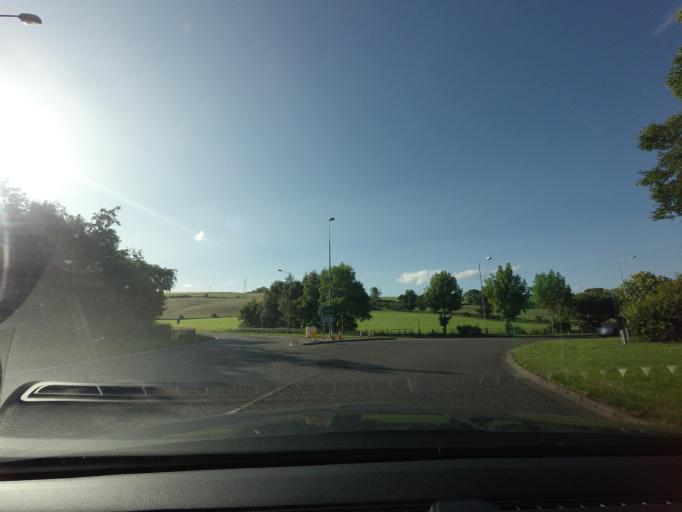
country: GB
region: Scotland
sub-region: Highland
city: Conon Bridge
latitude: 57.5791
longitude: -4.4384
